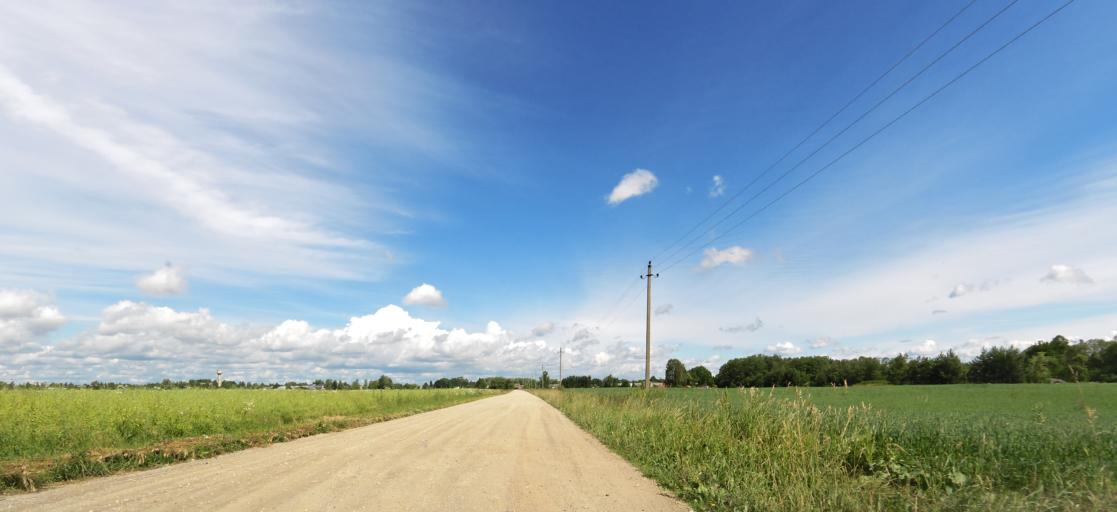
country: LT
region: Panevezys
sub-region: Birzai
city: Birzai
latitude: 56.1782
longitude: 24.7473
